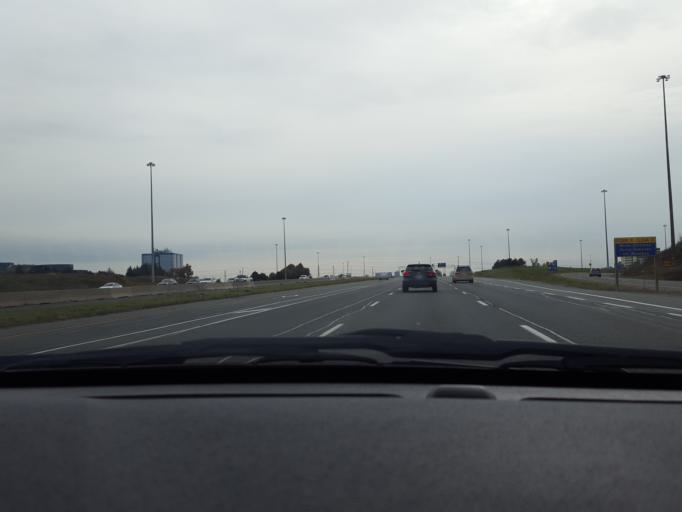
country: CA
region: Ontario
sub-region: York
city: Richmond Hill
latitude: 43.8514
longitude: -79.3723
